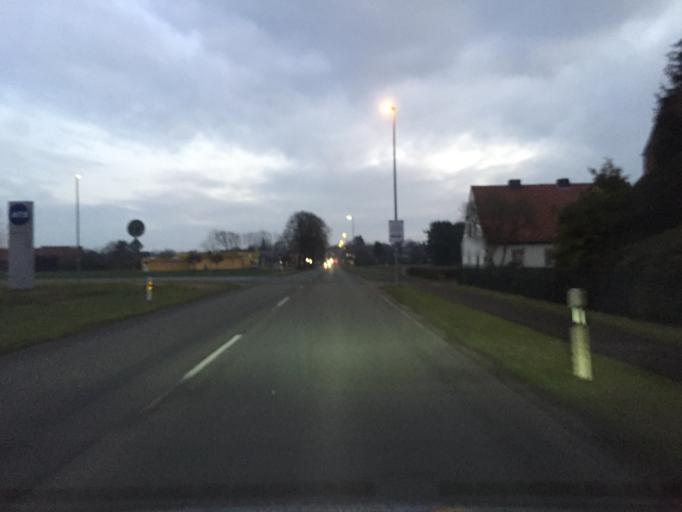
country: DE
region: Lower Saxony
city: Sulingen
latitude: 52.6755
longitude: 8.7885
